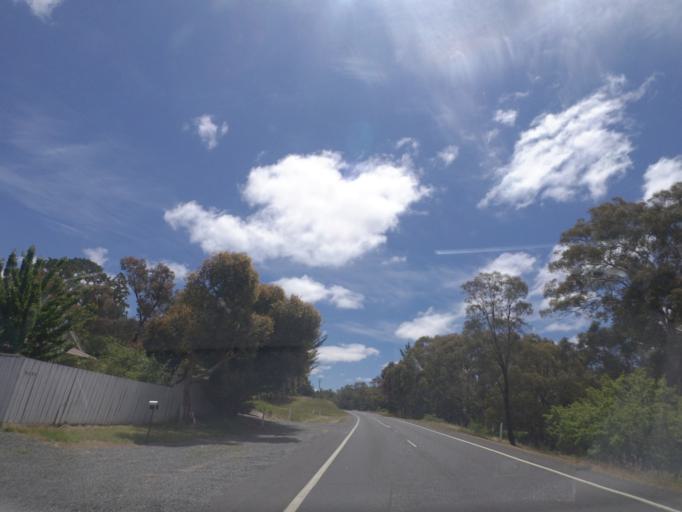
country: AU
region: Victoria
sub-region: Mount Alexander
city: Castlemaine
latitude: -37.2858
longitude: 144.1618
